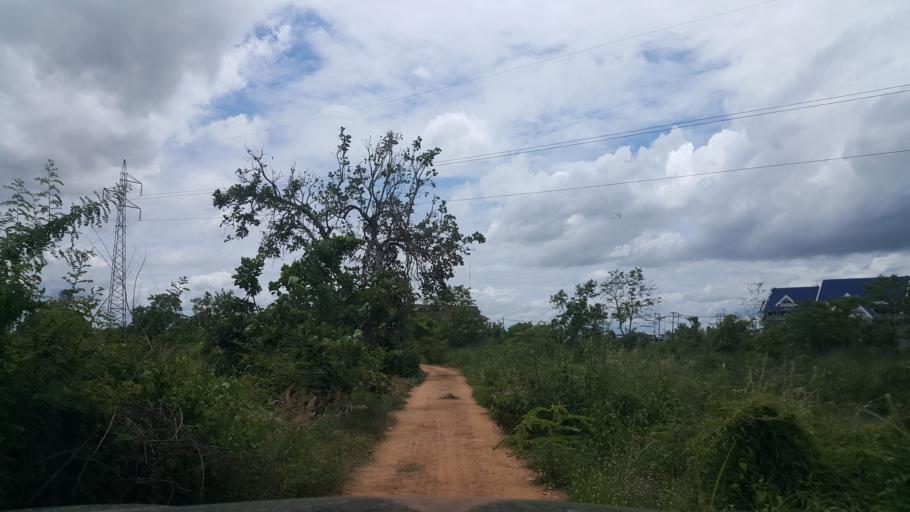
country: TH
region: Sukhothai
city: Sukhothai
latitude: 17.0333
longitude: 99.7990
